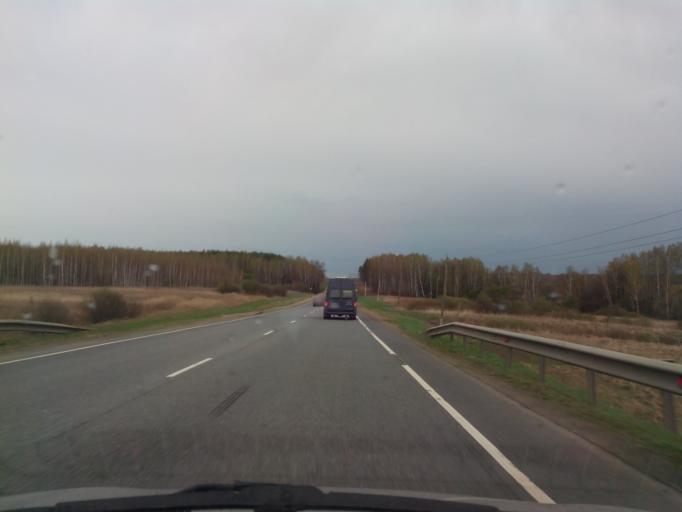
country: RU
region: Moskovskaya
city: Uzunovo
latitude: 54.5032
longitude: 38.5012
